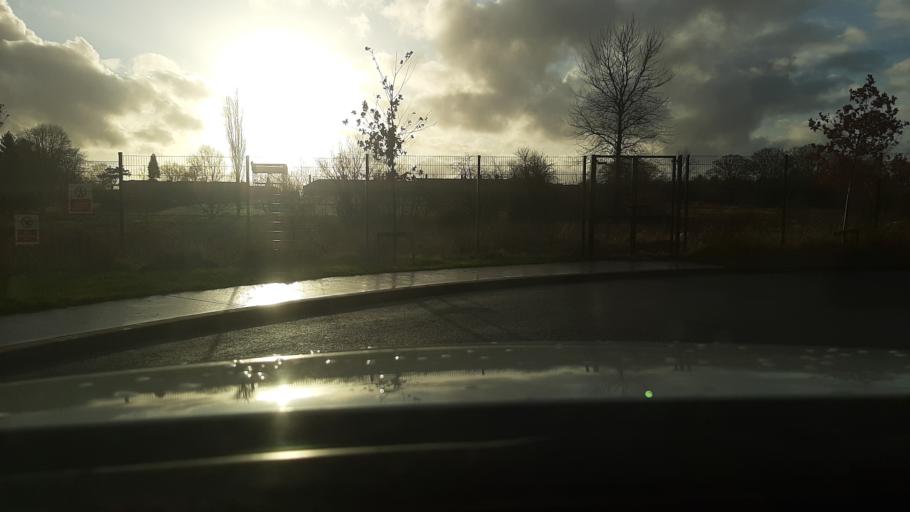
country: IE
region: Leinster
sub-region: Kildare
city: Kildare
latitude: 53.1581
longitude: -6.9010
